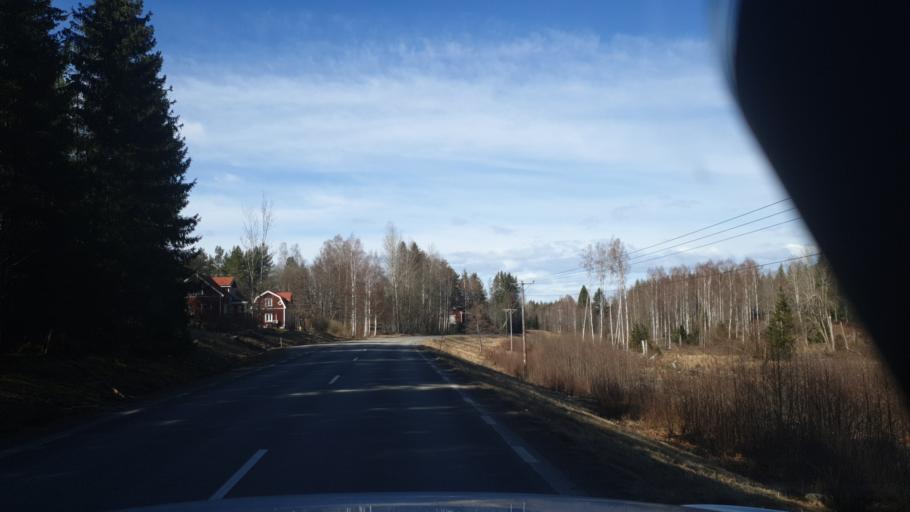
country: SE
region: Vaermland
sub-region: Arvika Kommun
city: Arvika
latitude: 59.7159
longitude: 12.5682
